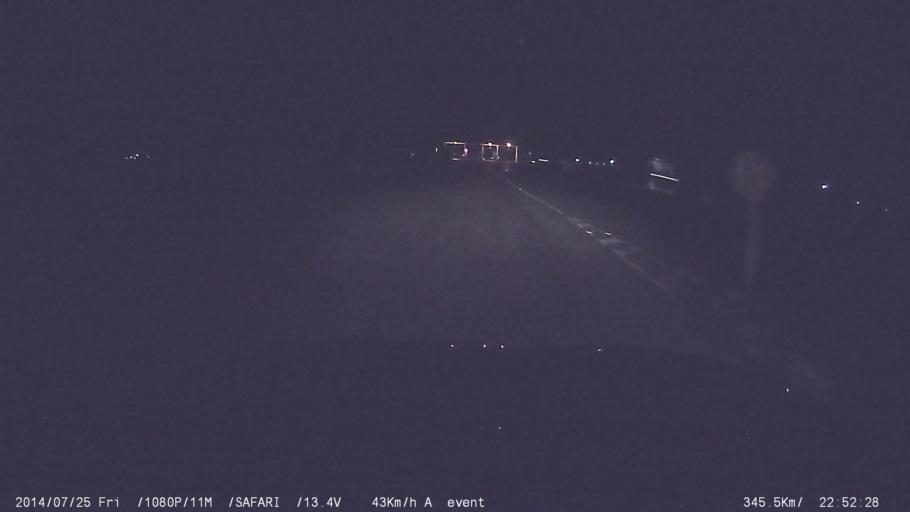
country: IN
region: Tamil Nadu
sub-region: Coimbatore
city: Irugur
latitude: 11.0068
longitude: 77.0702
